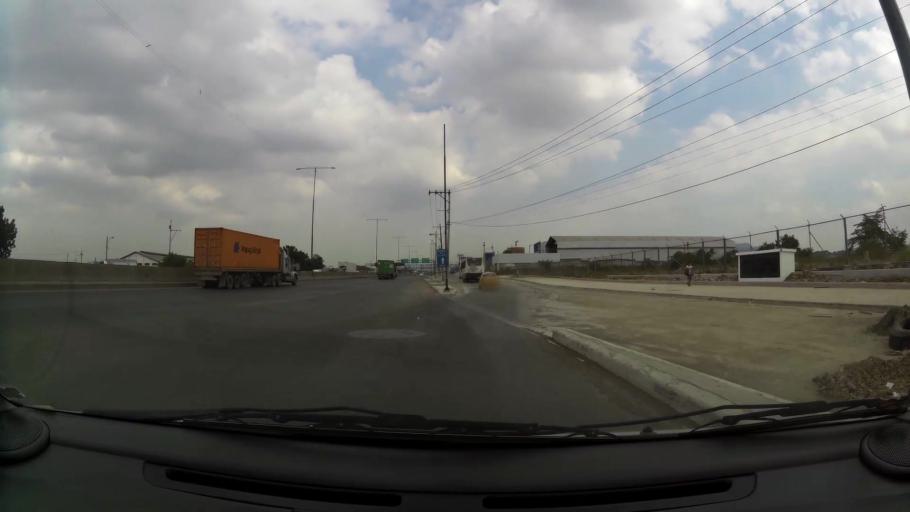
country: EC
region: Guayas
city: Santa Lucia
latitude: -2.1049
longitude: -79.9481
